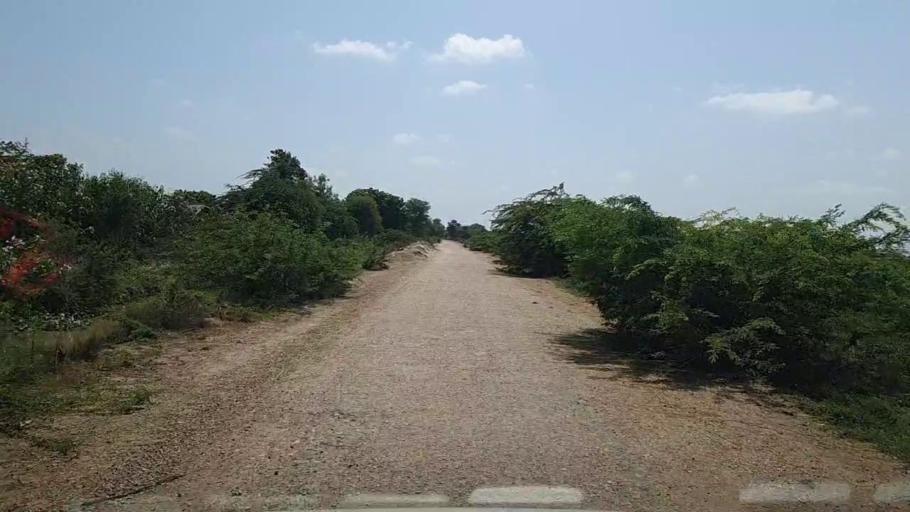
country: PK
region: Sindh
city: Kario
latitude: 24.8695
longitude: 68.6876
